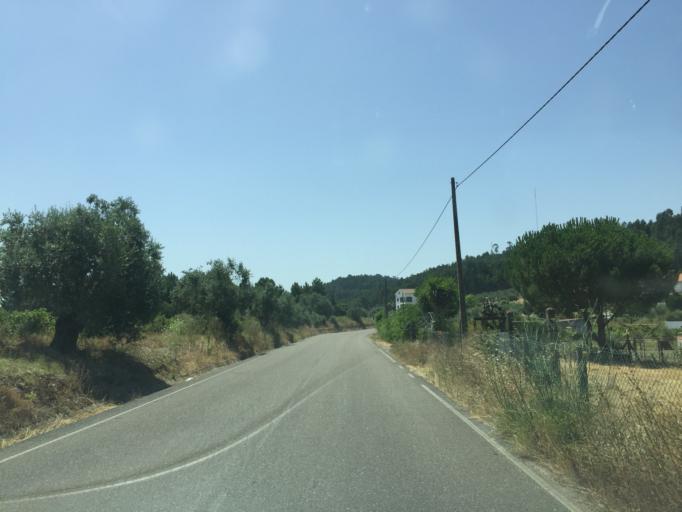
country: PT
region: Santarem
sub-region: Ferreira do Zezere
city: Ferreira do Zezere
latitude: 39.6160
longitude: -8.3117
